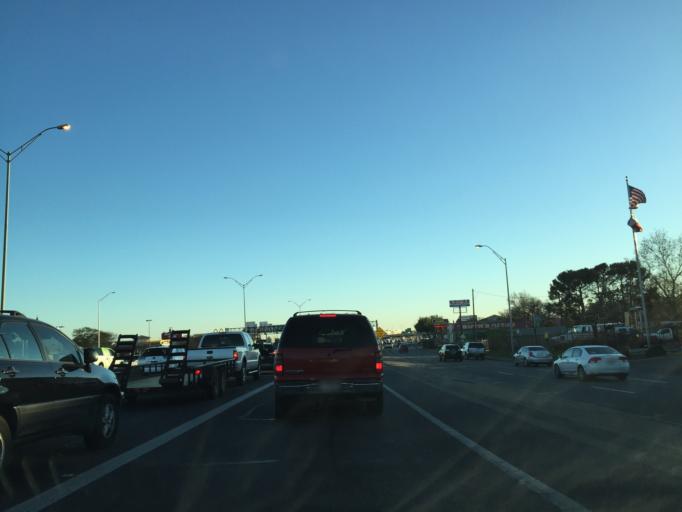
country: US
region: Texas
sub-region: Travis County
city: Austin
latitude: 30.3158
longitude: -97.7079
